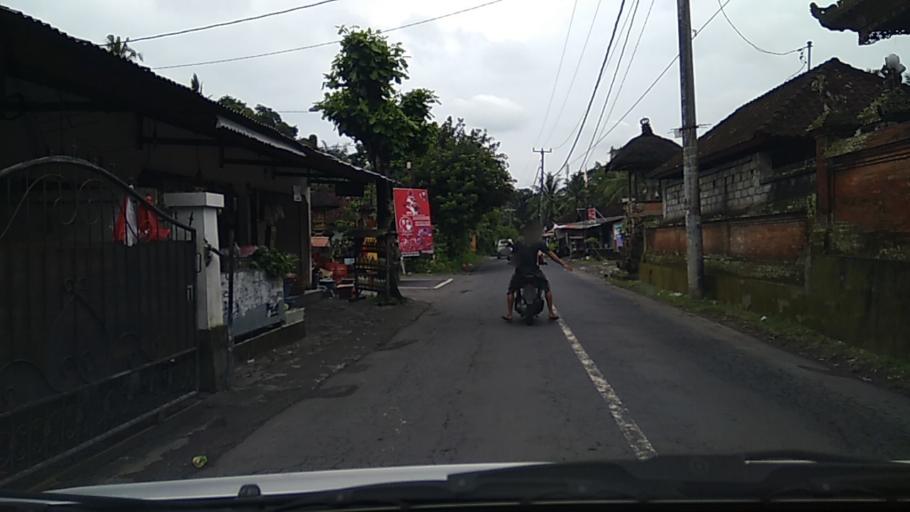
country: ID
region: Bali
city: Banjar Tebongkang
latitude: -8.5233
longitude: 115.2376
